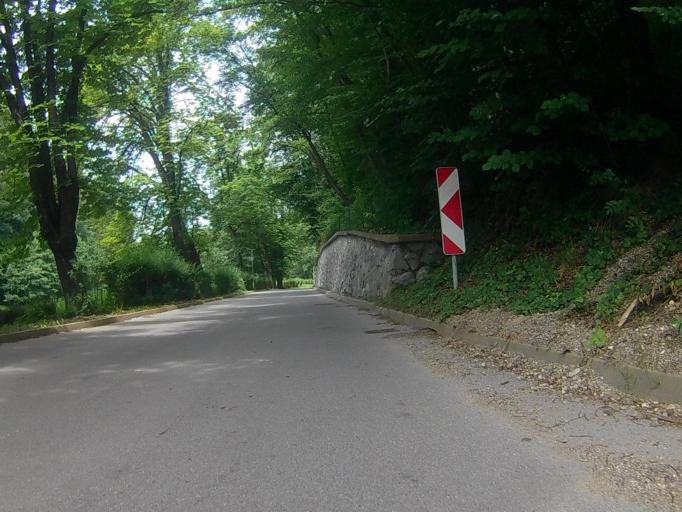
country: SI
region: Maribor
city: Maribor
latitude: 46.5697
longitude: 15.6485
